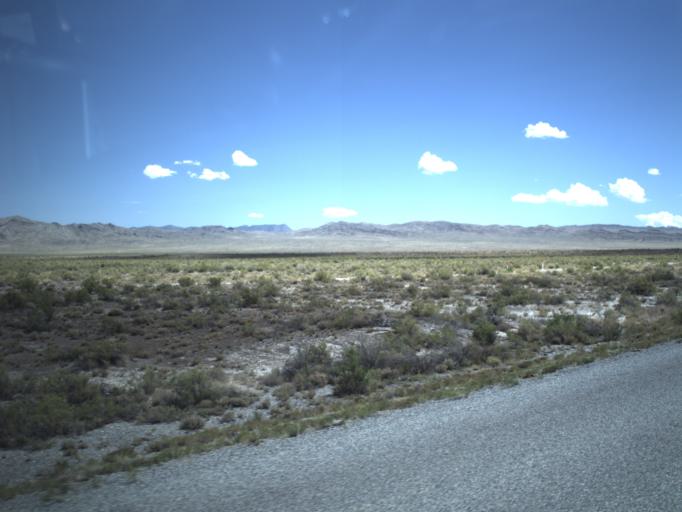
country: US
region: Nevada
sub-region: White Pine County
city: McGill
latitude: 39.0515
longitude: -113.9753
